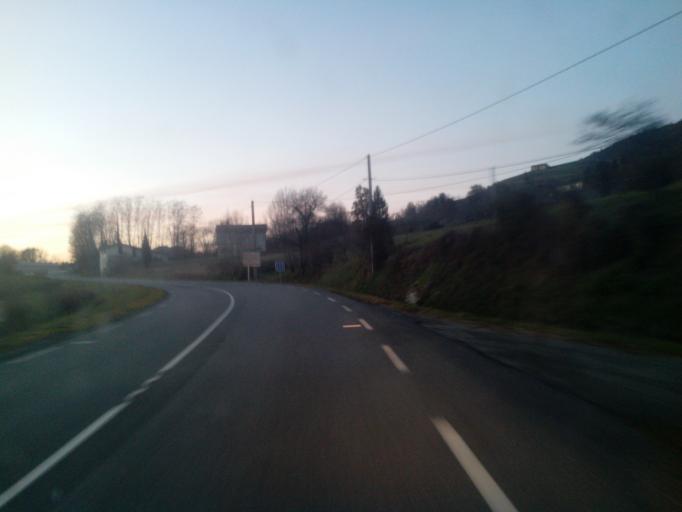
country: FR
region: Midi-Pyrenees
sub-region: Departement de l'Ariege
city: Foix
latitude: 42.9684
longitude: 1.5928
